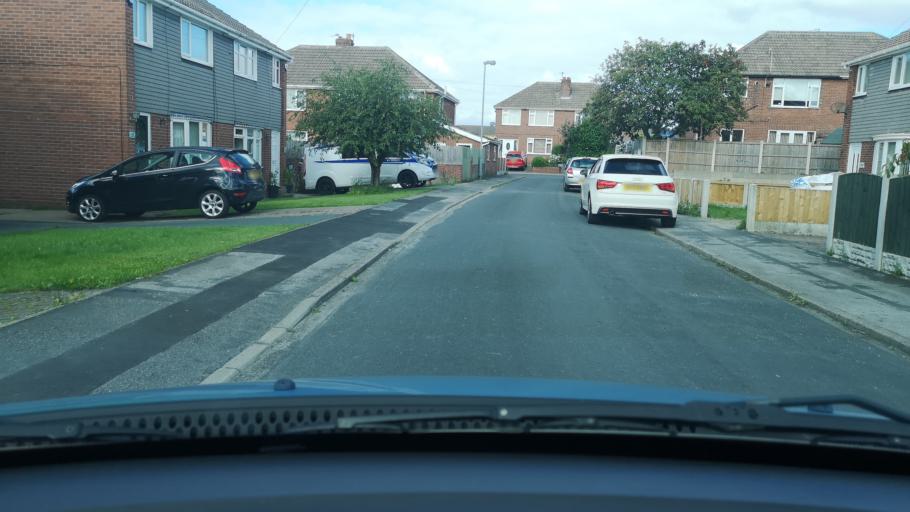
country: GB
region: England
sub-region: City and Borough of Wakefield
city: Featherstone
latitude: 53.6705
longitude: -1.3549
